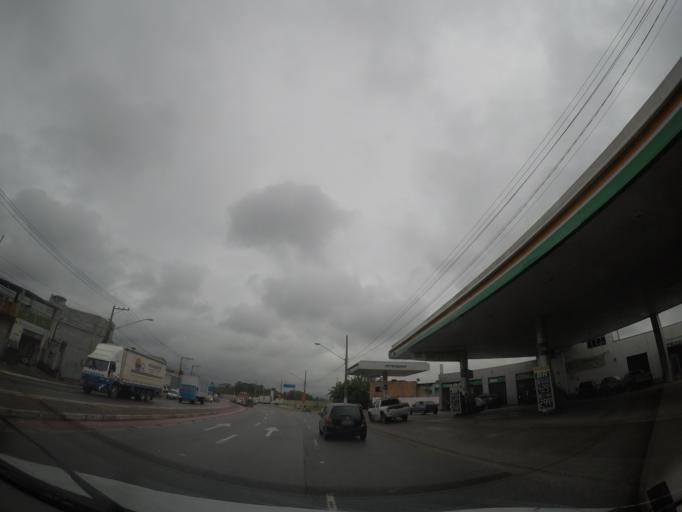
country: BR
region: Sao Paulo
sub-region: Guarulhos
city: Guarulhos
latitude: -23.4836
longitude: -46.4691
